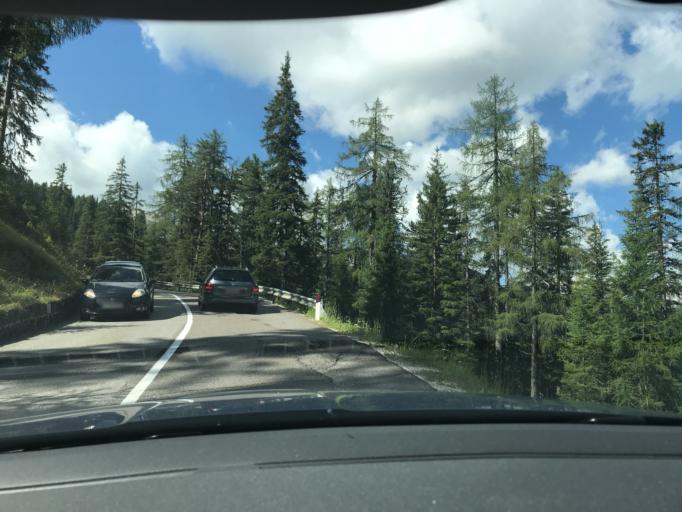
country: IT
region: Veneto
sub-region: Provincia di Belluno
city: Livinallongo del Col di Lana
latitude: 46.5517
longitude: 11.9776
